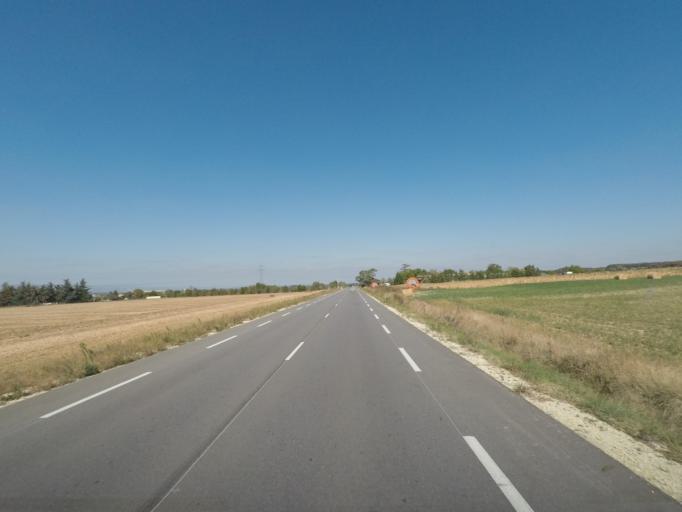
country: FR
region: Rhone-Alpes
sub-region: Departement de la Drome
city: Montmeyran
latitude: 44.8446
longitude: 5.0087
